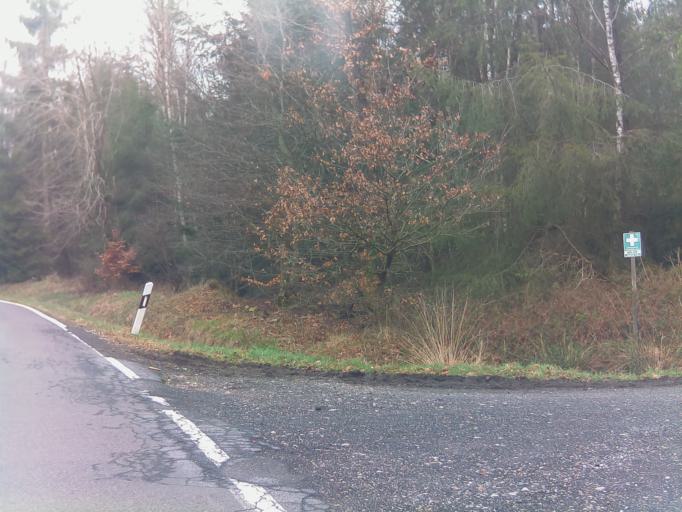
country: DE
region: Rheinland-Pfalz
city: Ippenschied
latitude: 49.8997
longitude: 7.6121
